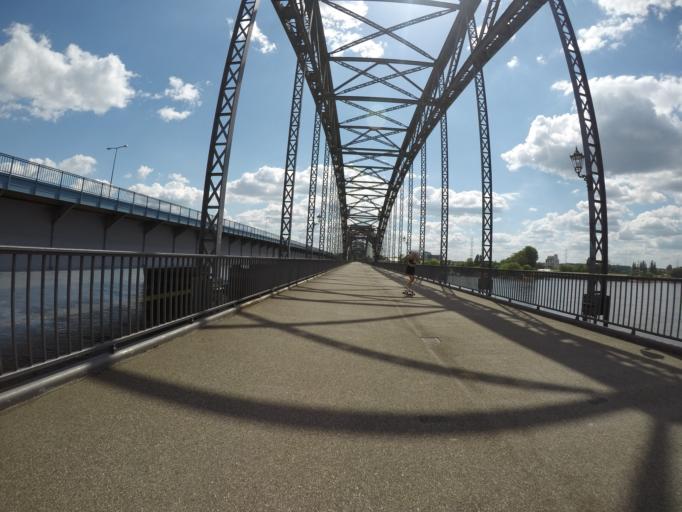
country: DE
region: Hamburg
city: Harburg
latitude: 53.4750
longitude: 9.9940
